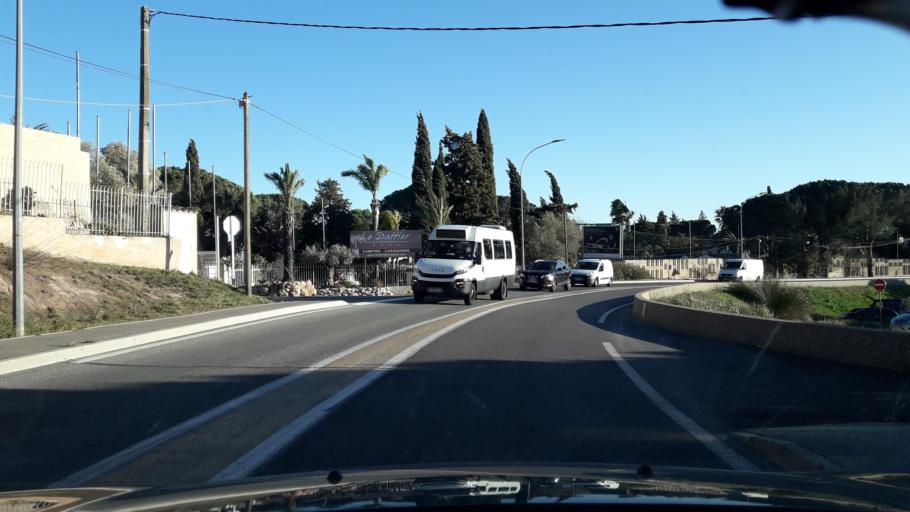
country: FR
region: Provence-Alpes-Cote d'Azur
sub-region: Departement du Var
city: Frejus
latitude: 43.4497
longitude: 6.7280
